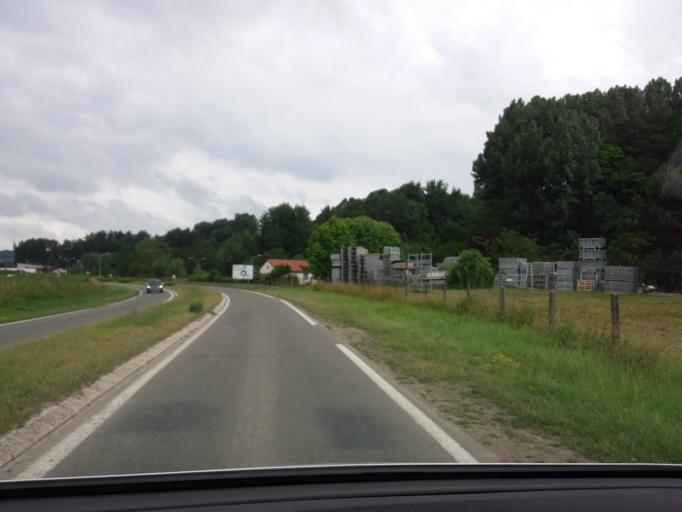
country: FR
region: Picardie
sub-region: Departement de l'Aisne
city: Bucy-le-Long
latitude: 49.3922
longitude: 3.3763
